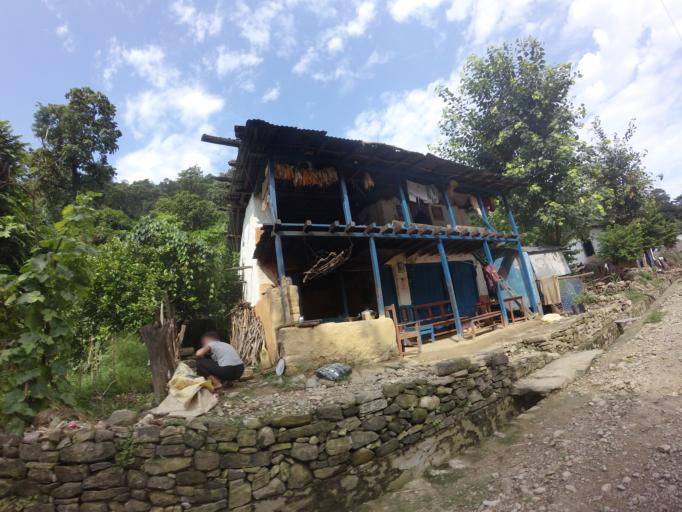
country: NP
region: Far Western
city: Tikapur
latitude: 28.6582
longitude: 81.2862
